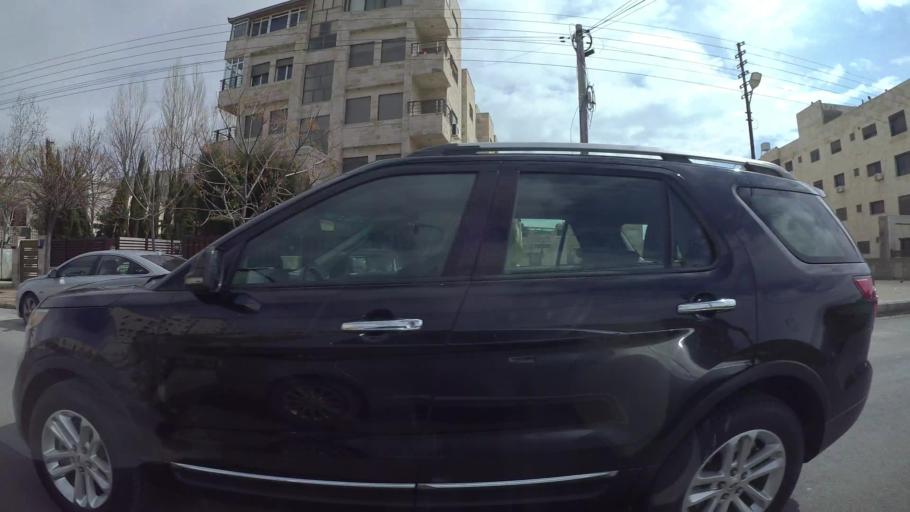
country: JO
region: Amman
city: Al Jubayhah
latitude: 31.9985
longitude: 35.8357
